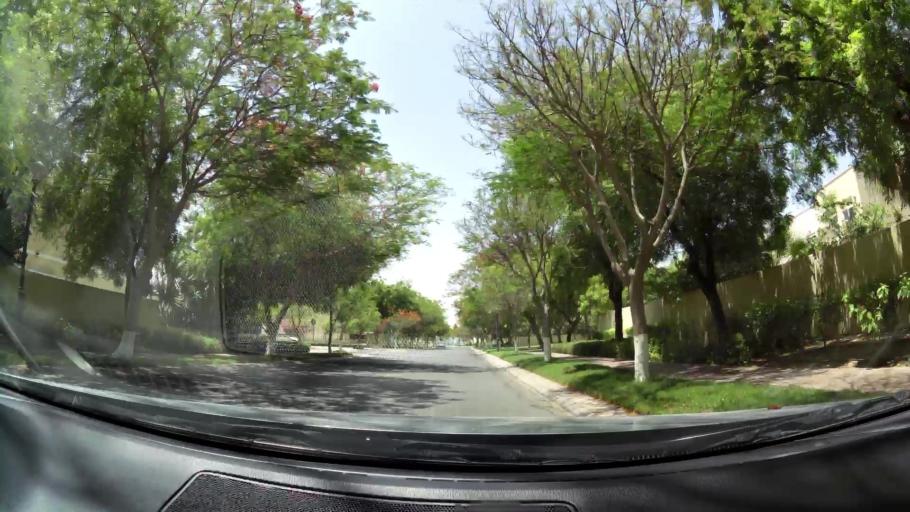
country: AE
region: Dubai
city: Dubai
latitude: 25.0481
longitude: 55.1738
